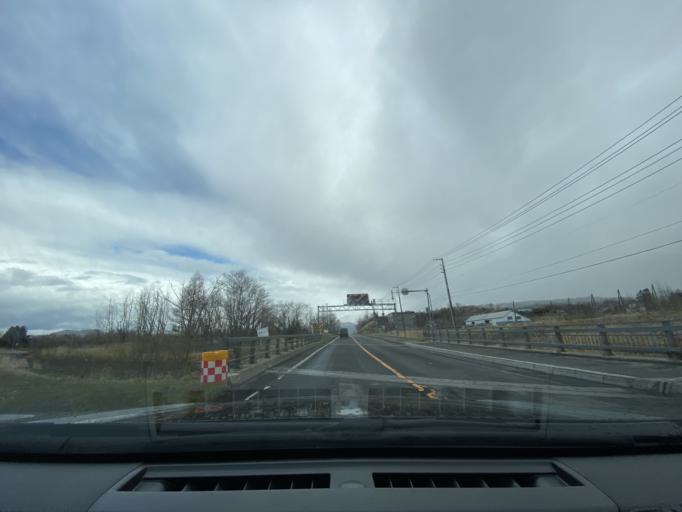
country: JP
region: Hokkaido
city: Fukagawa
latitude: 43.7013
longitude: 142.0741
